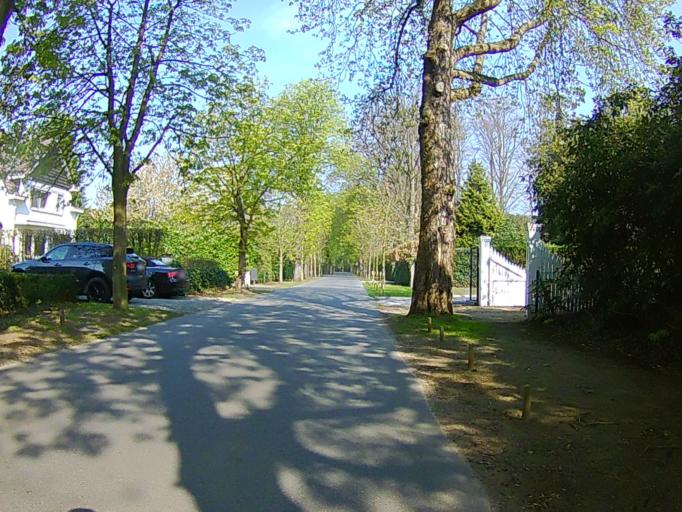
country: BE
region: Flanders
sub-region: Provincie Antwerpen
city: Kapellen
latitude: 51.3099
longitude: 4.4378
